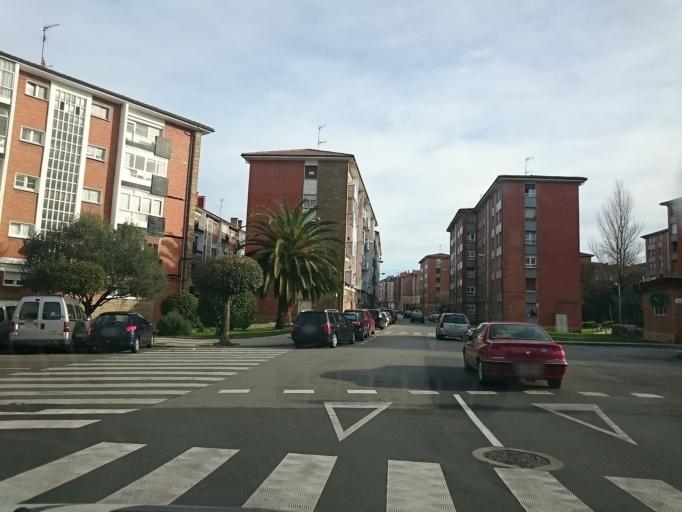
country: ES
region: Asturias
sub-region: Province of Asturias
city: Gijon
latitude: 43.5199
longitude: -5.6684
